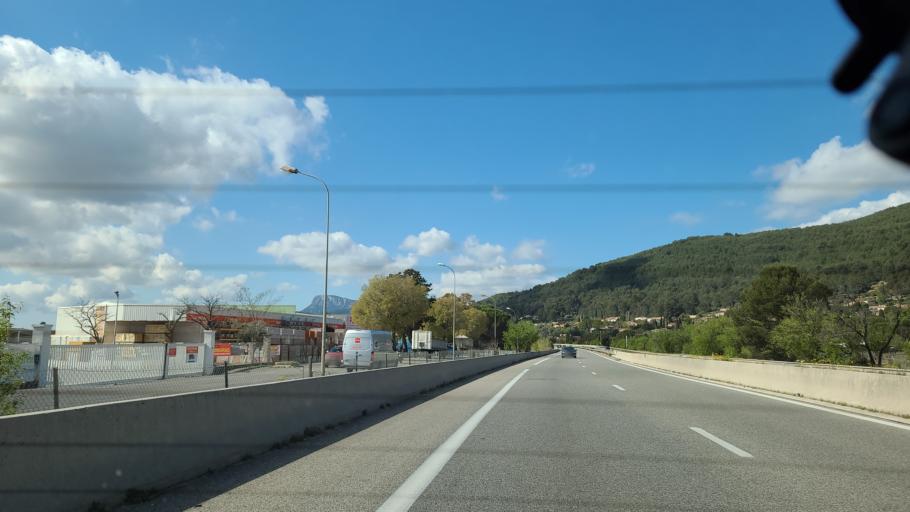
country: FR
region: Provence-Alpes-Cote d'Azur
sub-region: Departement du Var
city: Cuers
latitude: 43.2270
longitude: 6.0767
